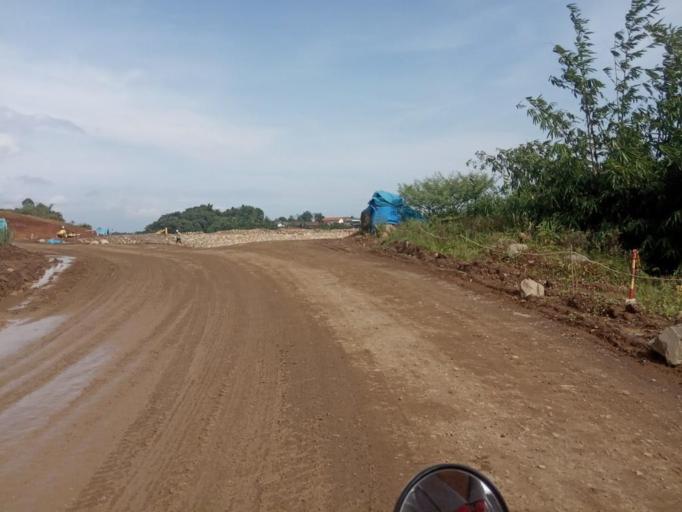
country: ID
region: West Java
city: Caringin
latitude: -6.6590
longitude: 106.8824
